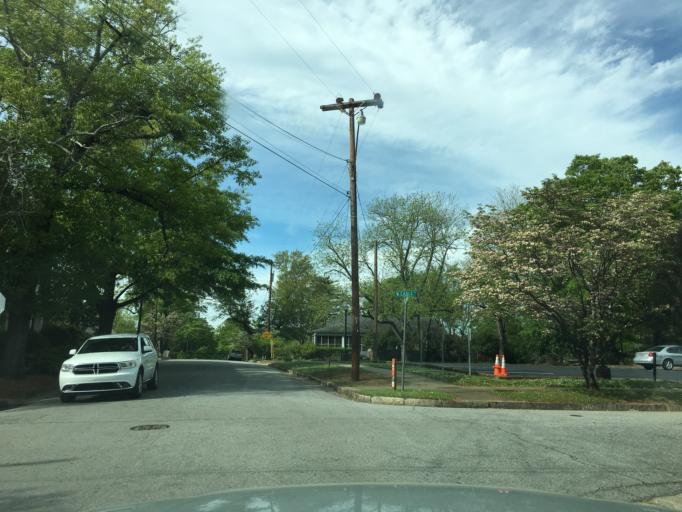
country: US
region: South Carolina
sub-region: Greenville County
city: Greenville
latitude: 34.8633
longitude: -82.4007
